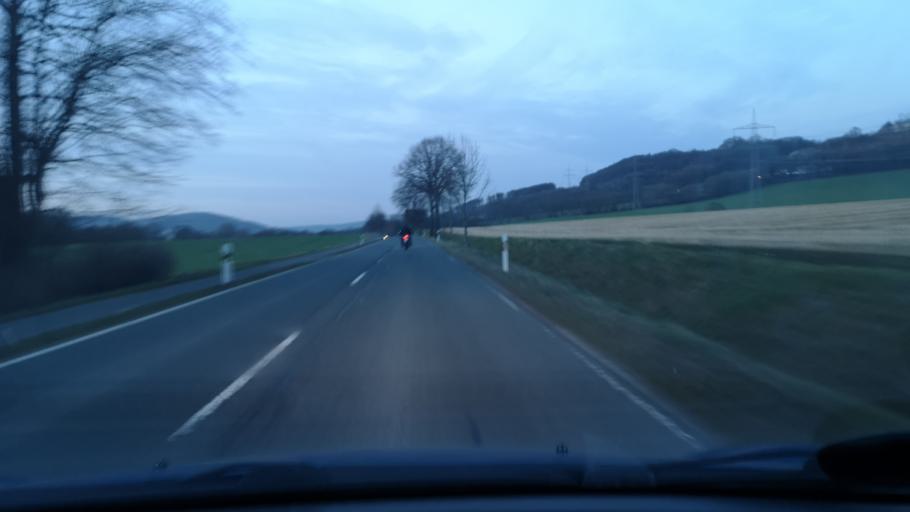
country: DE
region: Lower Saxony
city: Salzhemmendorf
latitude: 52.0503
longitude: 9.5956
